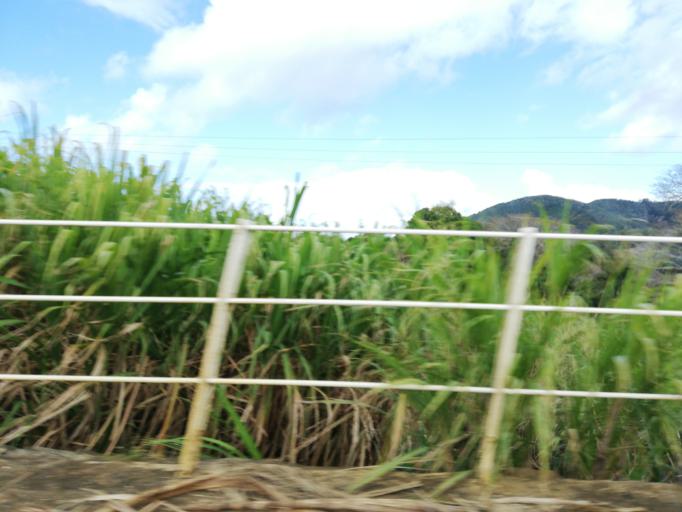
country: MU
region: Flacq
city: Grande Riviere Sud Est
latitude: -20.2773
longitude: 57.7599
